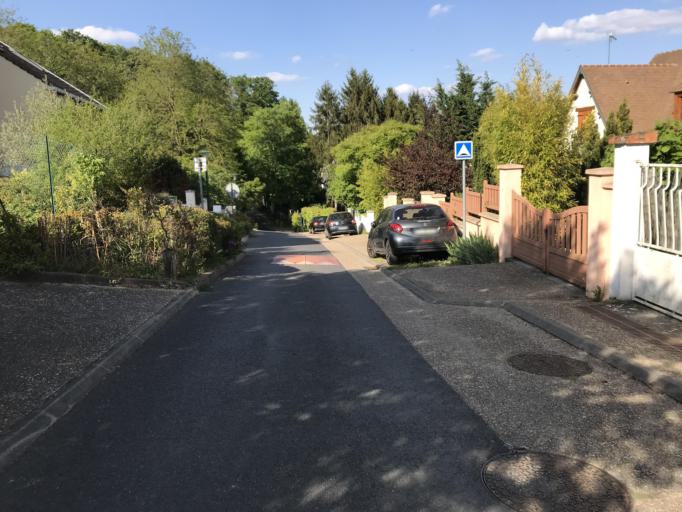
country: FR
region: Ile-de-France
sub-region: Departement des Hauts-de-Seine
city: Chatenay-Malabry
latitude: 48.7573
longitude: 2.2662
